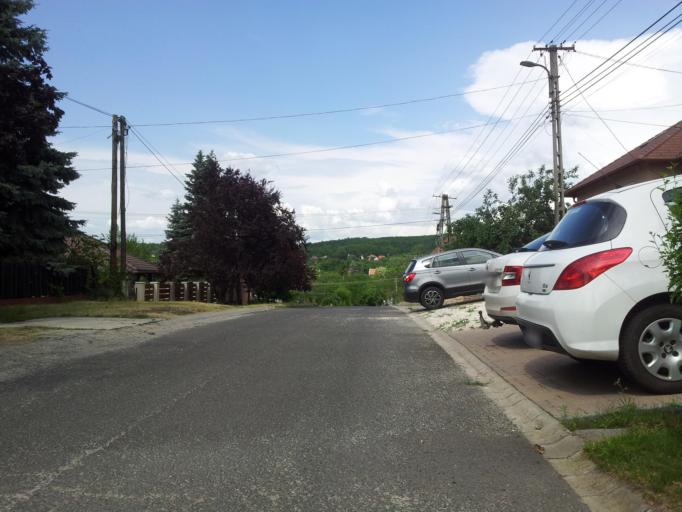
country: HU
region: Pest
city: Veresegyhaz
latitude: 47.6490
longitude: 19.3076
